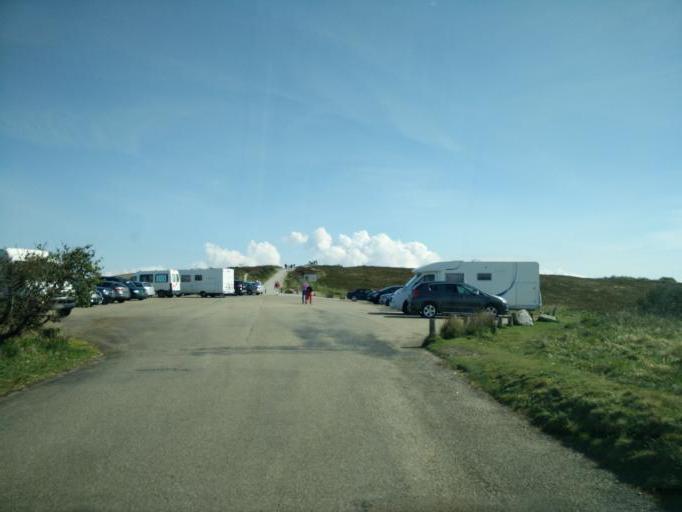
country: FR
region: Brittany
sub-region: Departement du Finistere
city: Plomodiern
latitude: 48.2181
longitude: -4.2367
